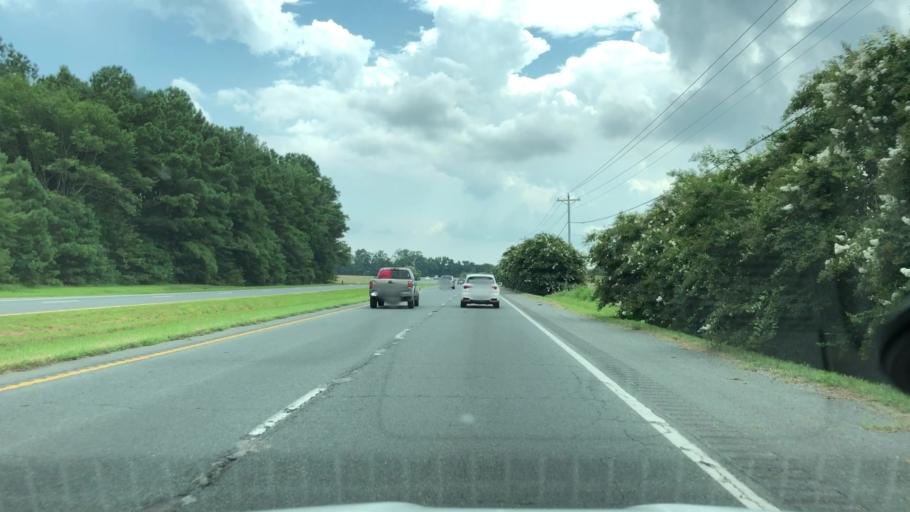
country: US
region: Virginia
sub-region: Accomack County
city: Accomac
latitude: 37.8098
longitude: -75.5941
